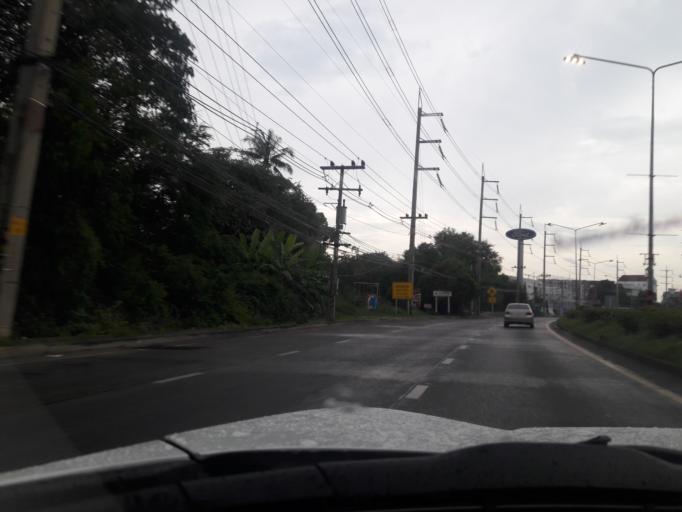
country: TH
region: Lop Buri
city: Lop Buri
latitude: 14.7995
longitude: 100.6595
